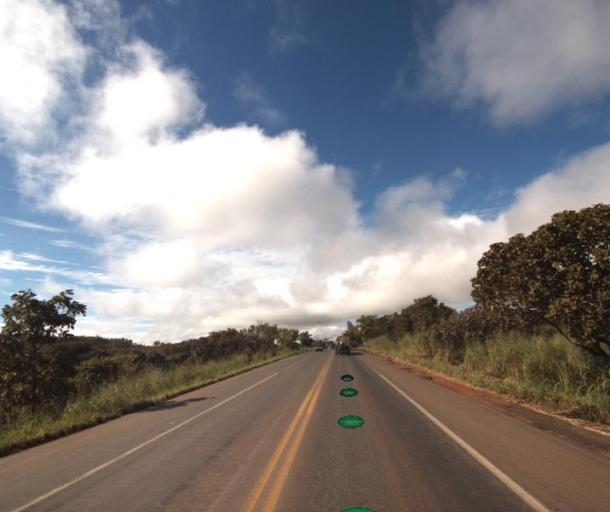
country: BR
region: Goias
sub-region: Uruacu
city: Uruacu
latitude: -14.5621
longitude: -49.1568
